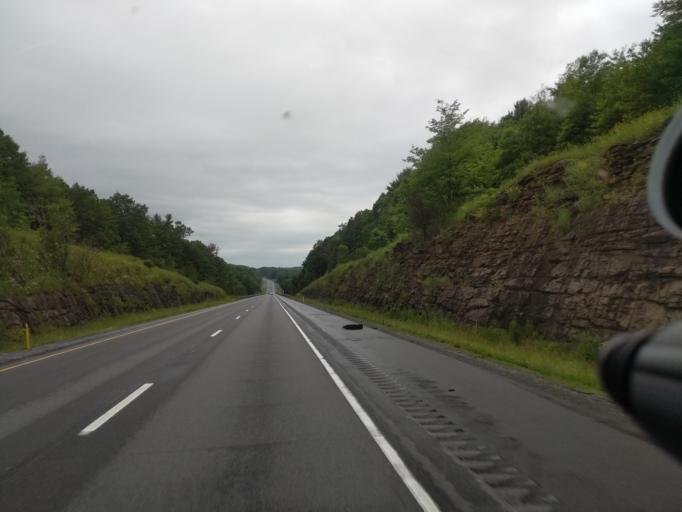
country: US
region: Pennsylvania
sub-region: Lycoming County
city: Jersey Shore
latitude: 41.0651
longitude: -77.2207
